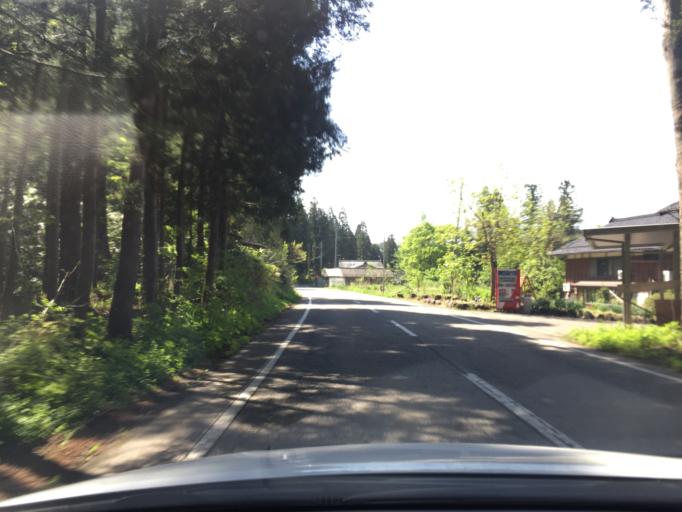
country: JP
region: Niigata
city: Kamo
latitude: 37.5662
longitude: 139.0848
